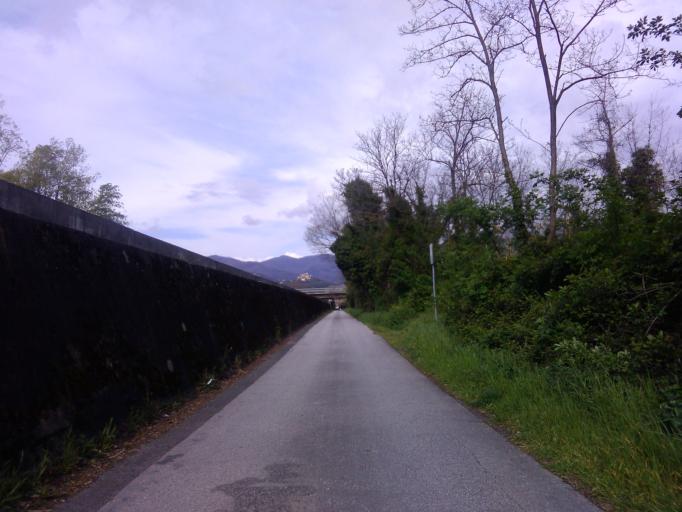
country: IT
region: Tuscany
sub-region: Provincia di Massa-Carrara
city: Marina di Carrara
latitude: 44.0534
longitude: 10.0248
